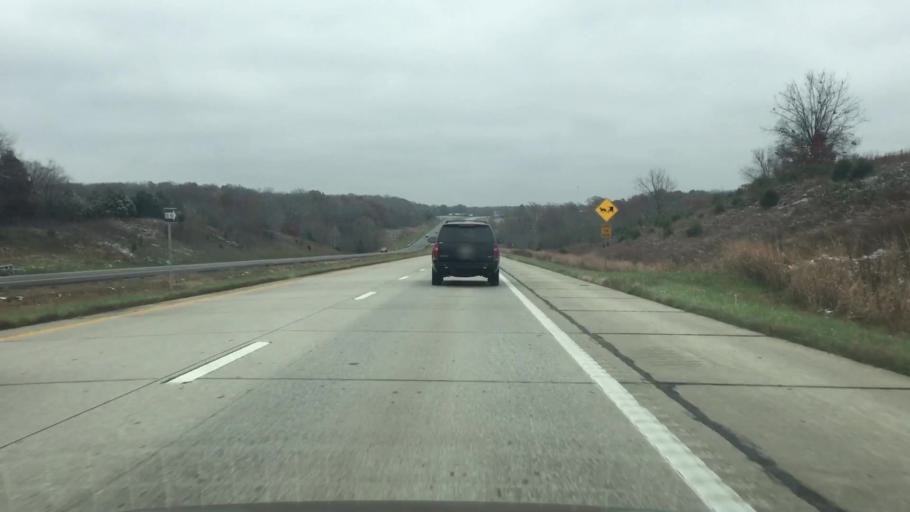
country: US
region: Missouri
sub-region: Saint Clair County
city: Osceola
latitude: 38.0211
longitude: -93.6690
